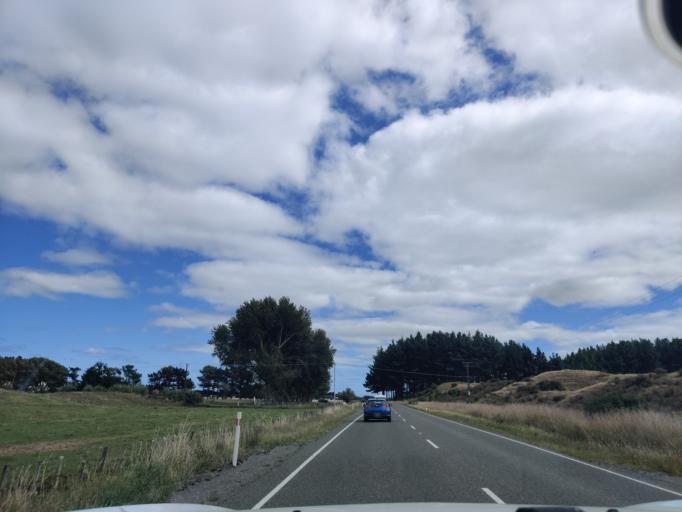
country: NZ
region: Manawatu-Wanganui
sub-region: Horowhenua District
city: Foxton
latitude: -40.4191
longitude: 175.4275
